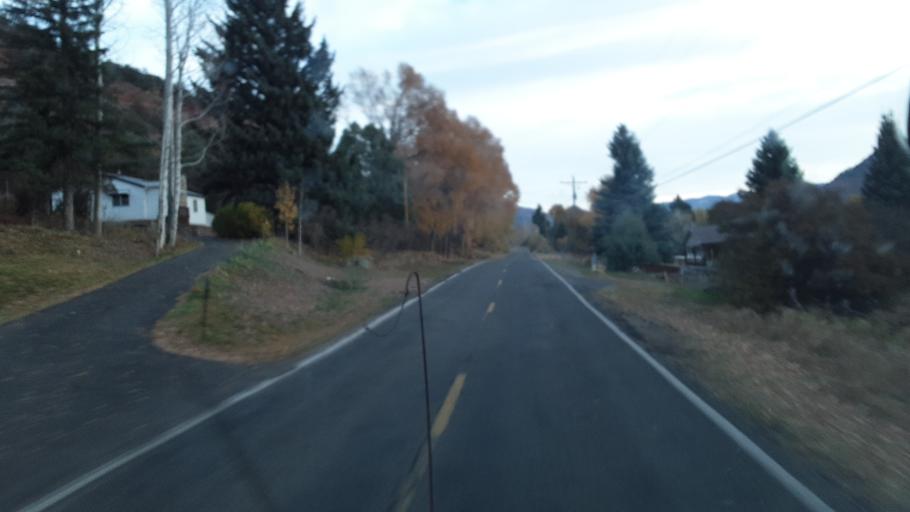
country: US
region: Colorado
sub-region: La Plata County
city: Durango
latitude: 37.3512
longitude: -107.8570
